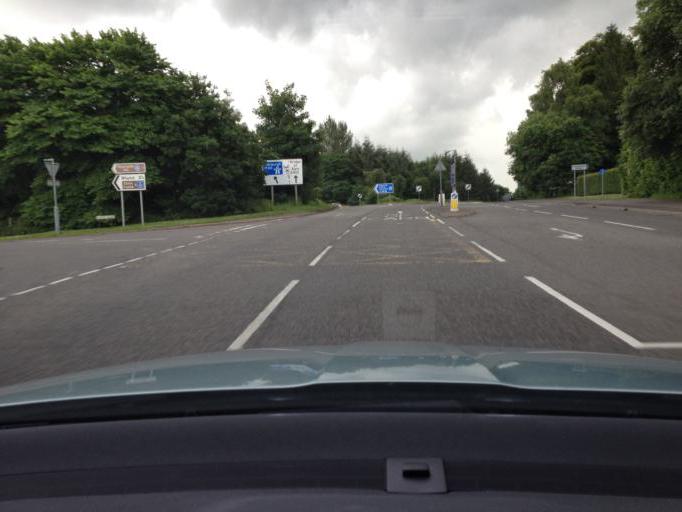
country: GB
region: Scotland
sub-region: Perth and Kinross
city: Perth
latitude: 56.3730
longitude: -3.4239
